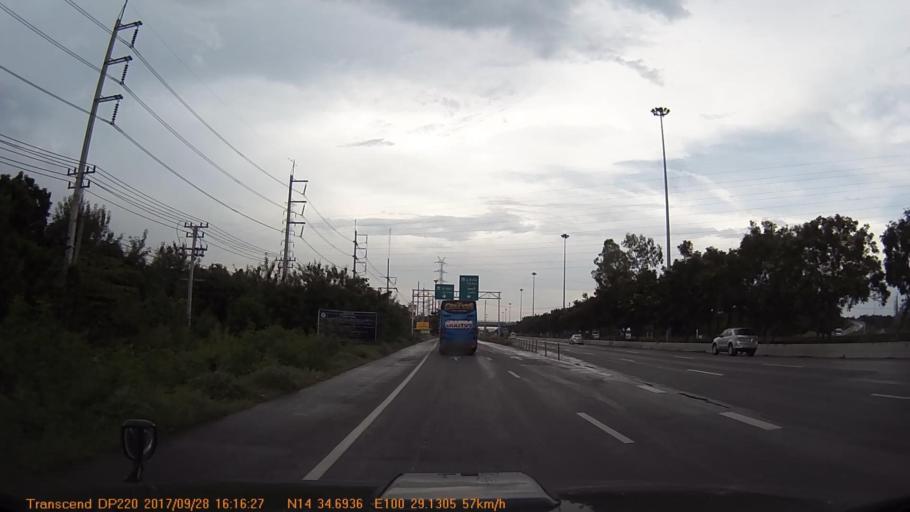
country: TH
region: Ang Thong
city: Ang Thong
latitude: 14.5785
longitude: 100.4853
